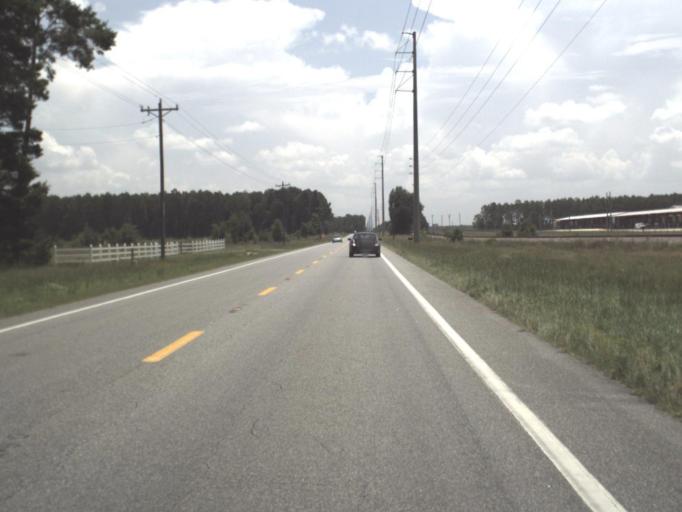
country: US
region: Florida
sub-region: Madison County
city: Madison
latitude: 30.4055
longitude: -83.2417
